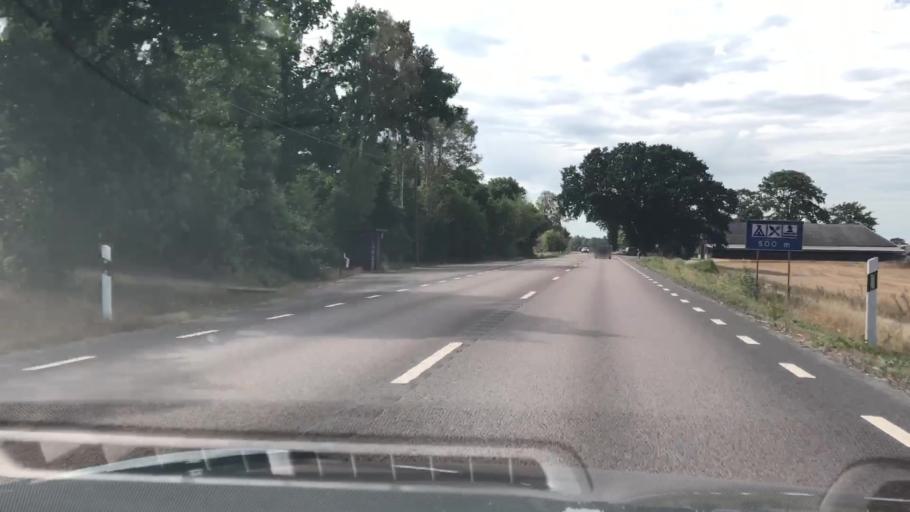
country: SE
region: Kalmar
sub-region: Torsas Kommun
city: Torsas
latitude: 56.3710
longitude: 16.0674
